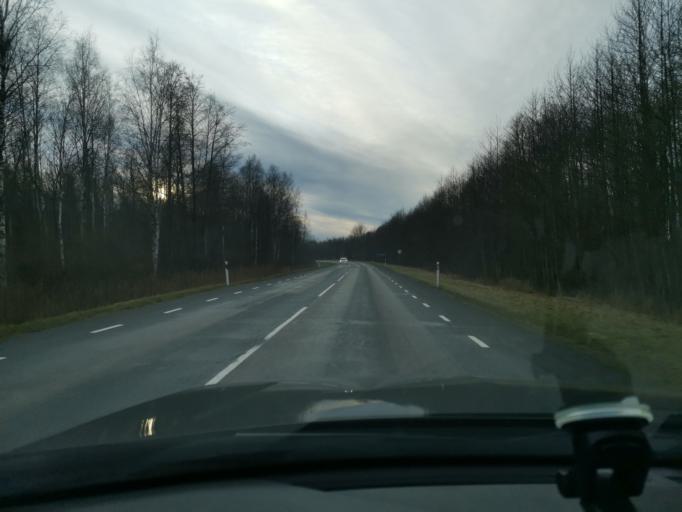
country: EE
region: Ida-Virumaa
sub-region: Sillamaee linn
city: Sillamae
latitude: 59.3247
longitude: 27.9219
